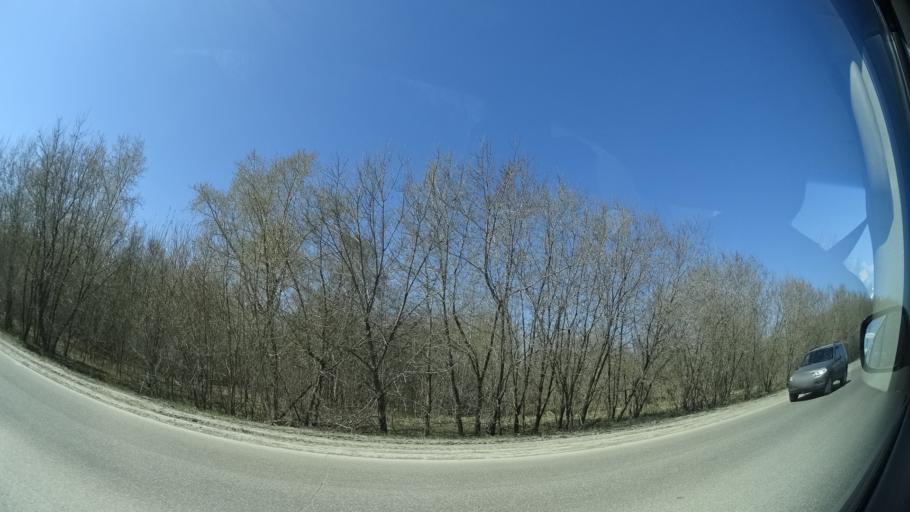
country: RU
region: Perm
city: Perm
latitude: 58.0950
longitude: 56.3170
